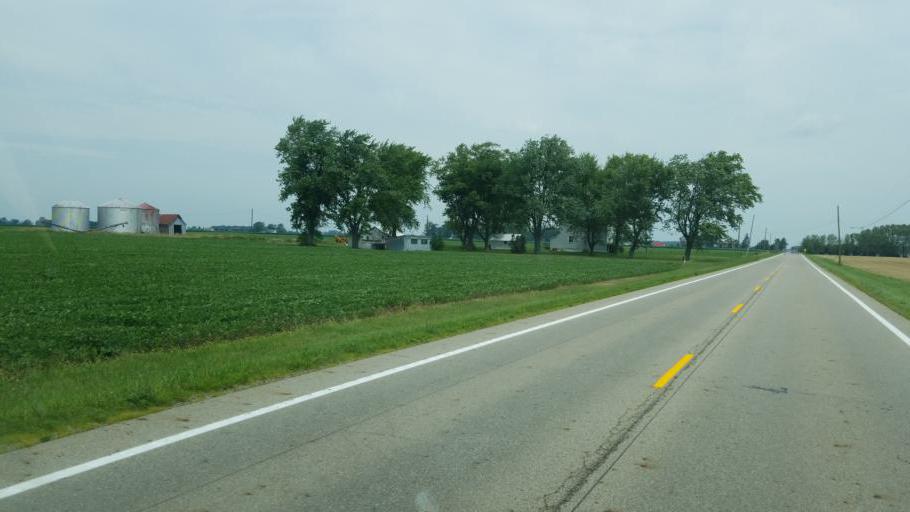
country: US
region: Ohio
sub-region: Madison County
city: Plain City
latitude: 40.0370
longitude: -83.2994
